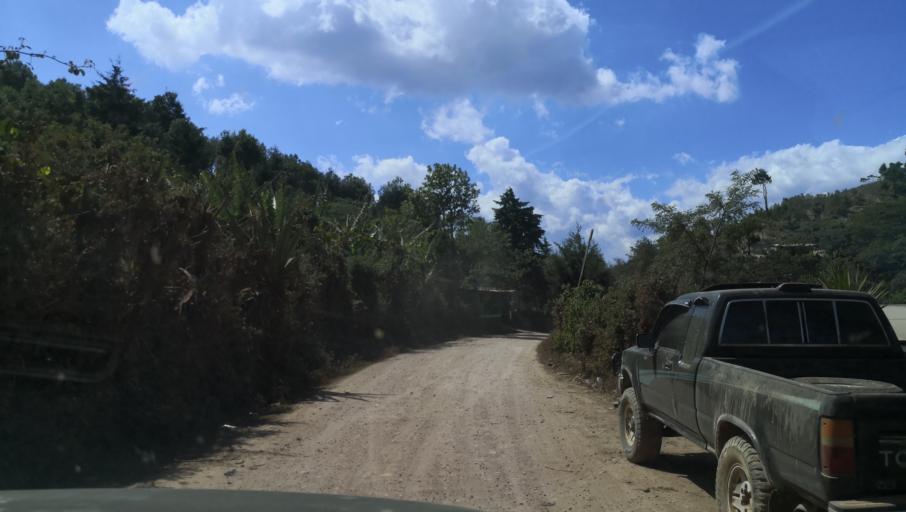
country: GT
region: Jalapa
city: San Carlos Alzatate
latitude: 14.4023
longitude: -89.9817
